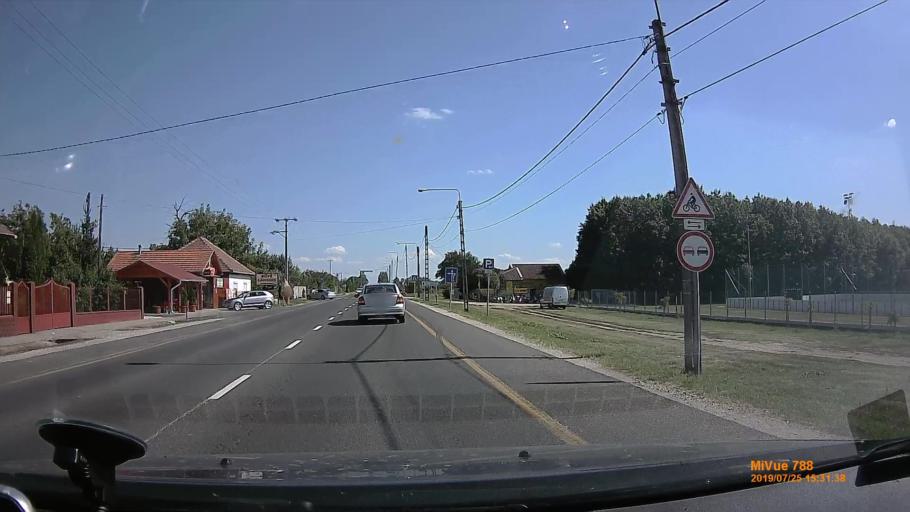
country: HU
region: Borsod-Abauj-Zemplen
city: Malyi
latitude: 48.0122
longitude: 20.8250
